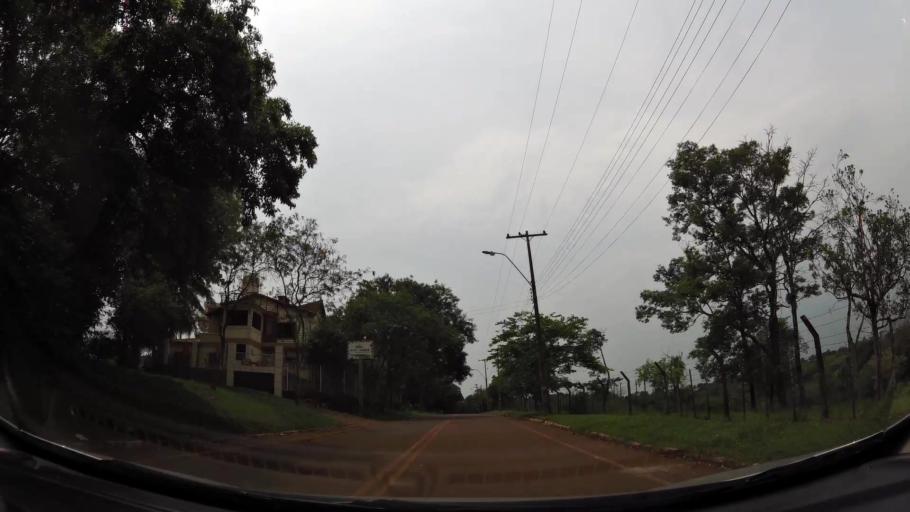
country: PY
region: Alto Parana
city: Presidente Franco
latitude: -25.5590
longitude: -54.6303
